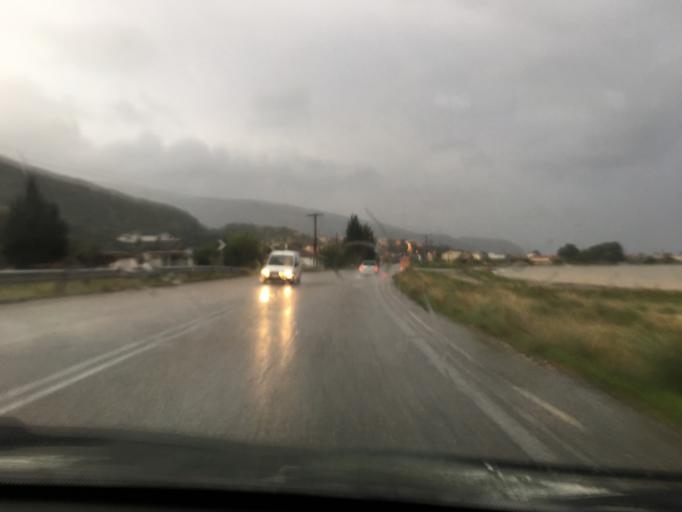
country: GR
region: West Greece
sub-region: Nomos Aitolias kai Akarnanias
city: Nafpaktos
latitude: 38.3737
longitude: 21.7854
